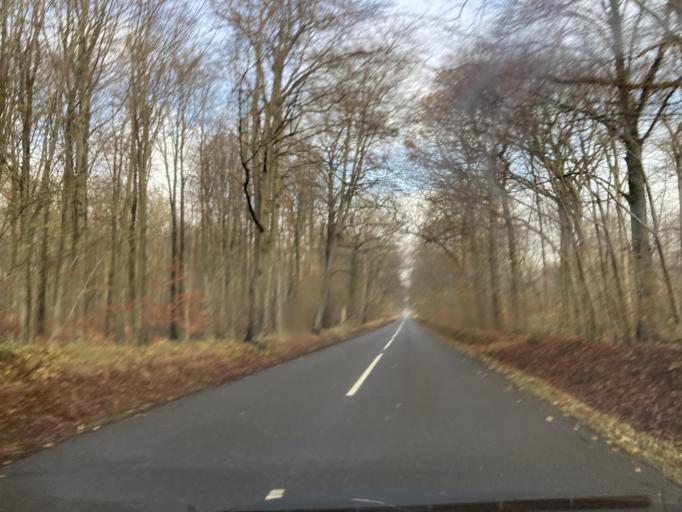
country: DK
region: Zealand
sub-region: Lolland Kommune
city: Rodby
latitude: 54.7789
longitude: 11.3696
